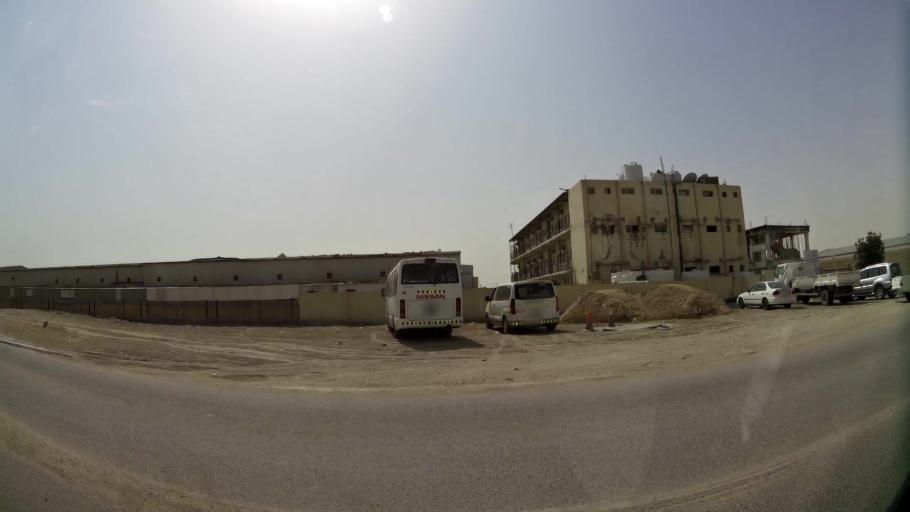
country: QA
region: Al Wakrah
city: Al Wukayr
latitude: 25.1711
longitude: 51.4663
